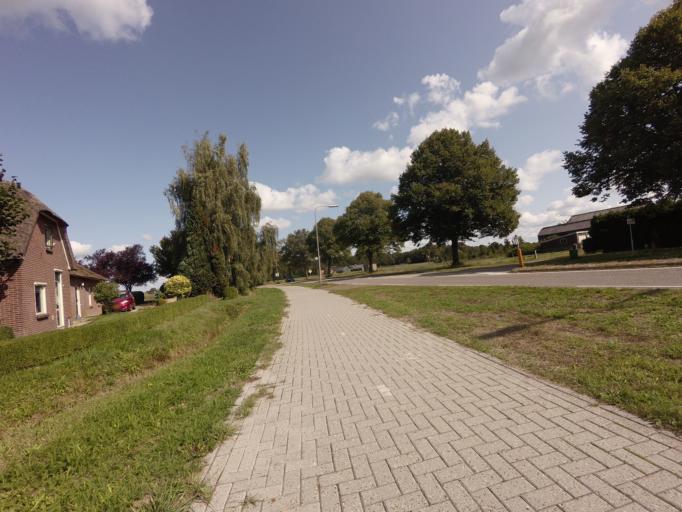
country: NL
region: Overijssel
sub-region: Gemeente Dalfsen
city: Dalfsen
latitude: 52.5288
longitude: 6.2611
